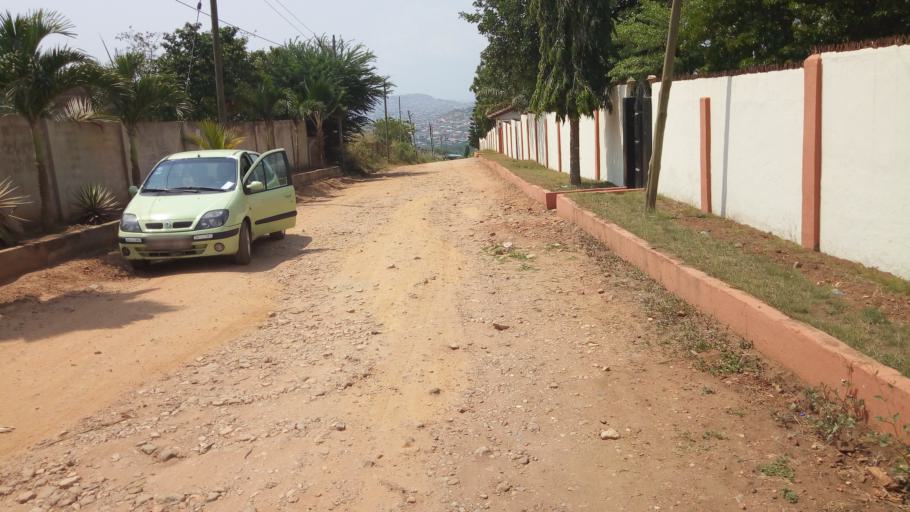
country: GH
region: Greater Accra
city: Gbawe
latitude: 5.5631
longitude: -0.3029
